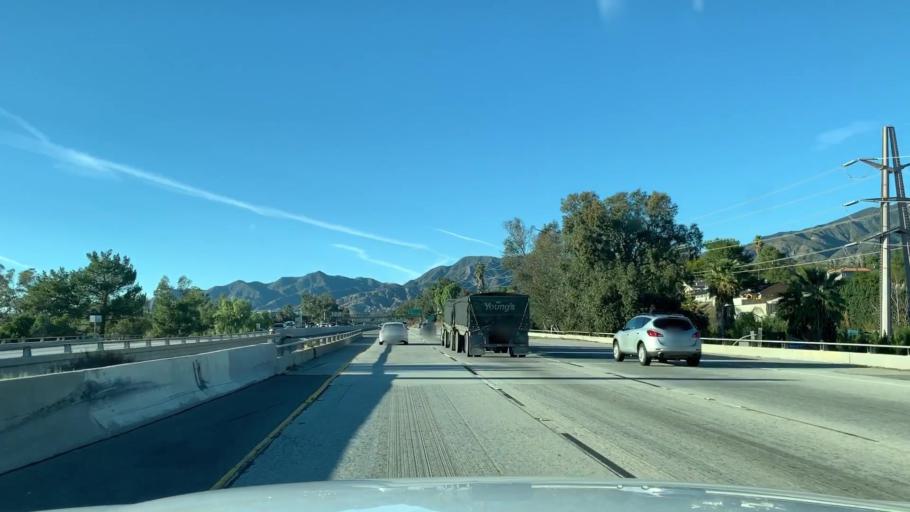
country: US
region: California
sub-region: Los Angeles County
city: San Fernando
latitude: 34.2991
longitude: -118.4189
